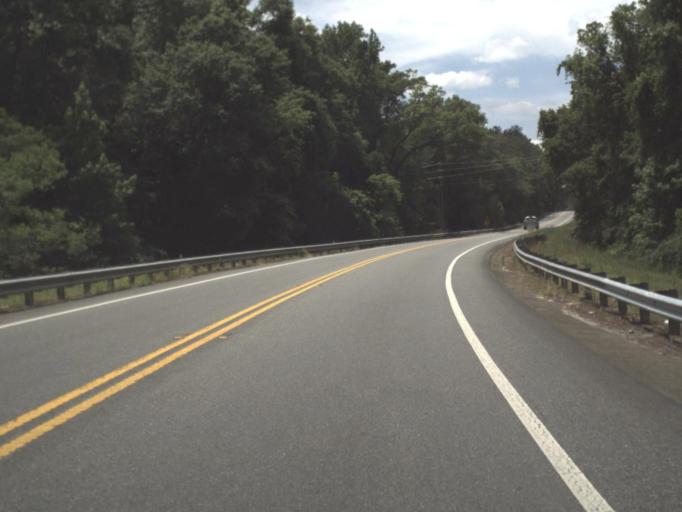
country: US
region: Florida
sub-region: Calhoun County
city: Blountstown
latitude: 30.4374
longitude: -85.0471
